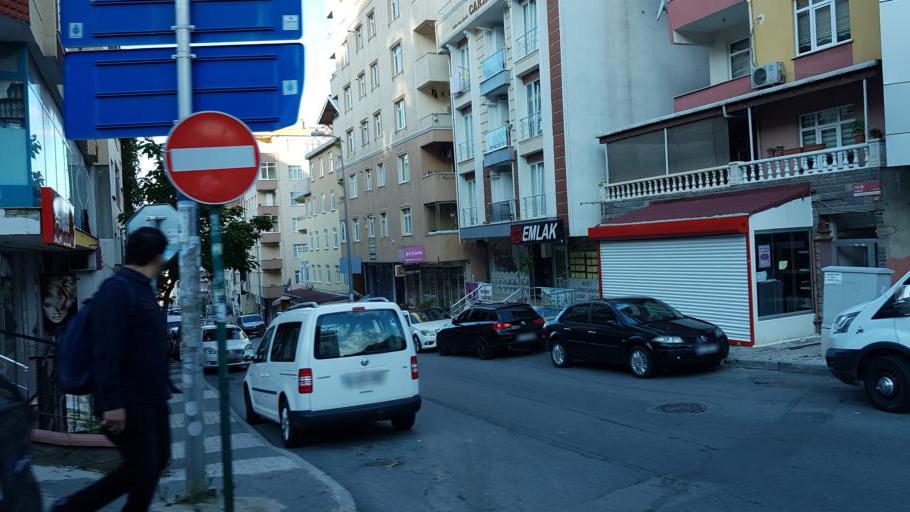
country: TR
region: Istanbul
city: Maltepe
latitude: 40.9416
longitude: 29.1536
